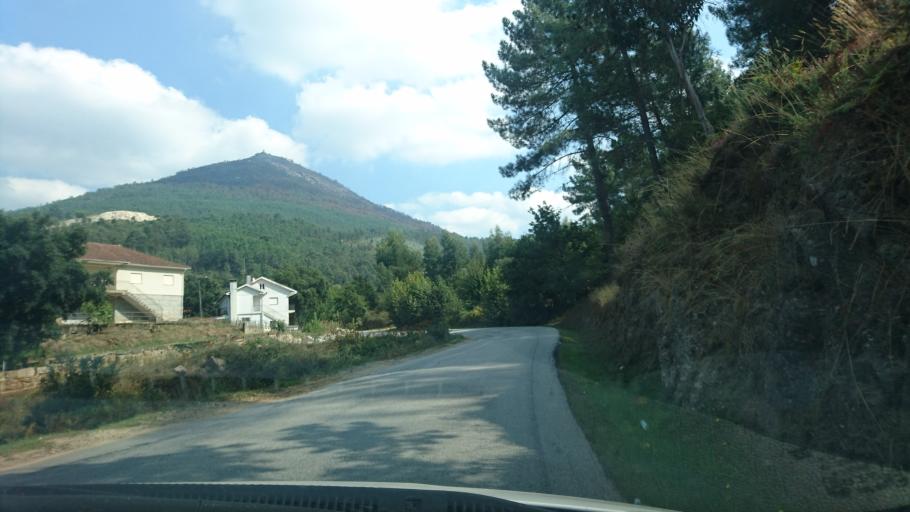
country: PT
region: Vila Real
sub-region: Mondim de Basto
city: Mondim de Basto
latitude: 41.4176
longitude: -7.9414
